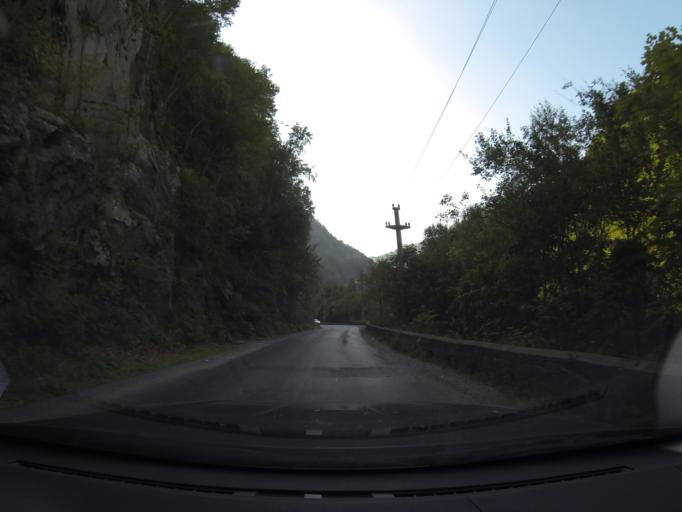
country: RO
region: Arges
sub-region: Comuna Arefu
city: Arefu
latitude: 45.3535
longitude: 24.6314
